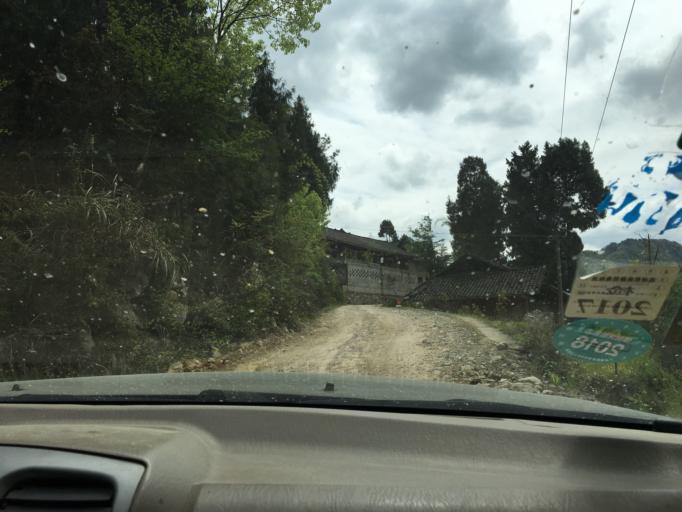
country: CN
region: Guizhou Sheng
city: Kuanping
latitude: 28.0230
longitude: 108.0683
